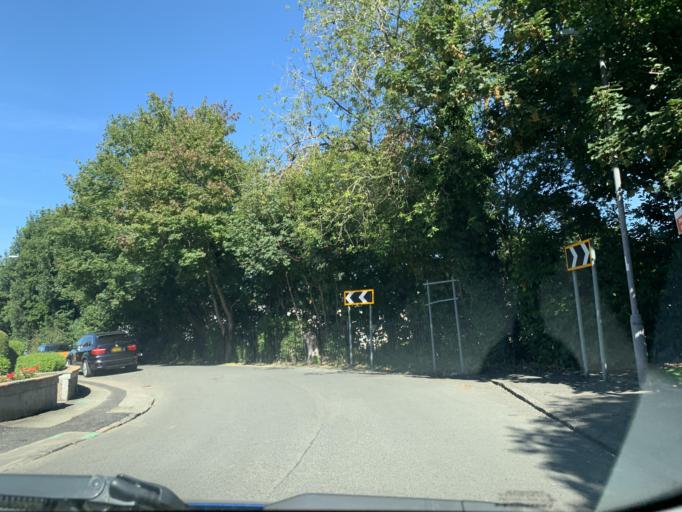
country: GB
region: Scotland
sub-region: East Renfrewshire
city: Giffnock
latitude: 55.8116
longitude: -4.2839
